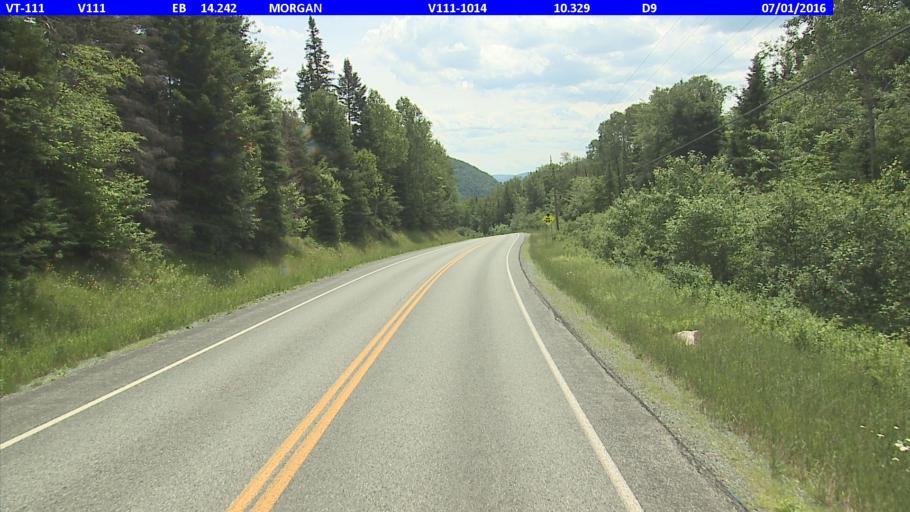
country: US
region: Vermont
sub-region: Orleans County
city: Newport
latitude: 44.8551
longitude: -71.9190
